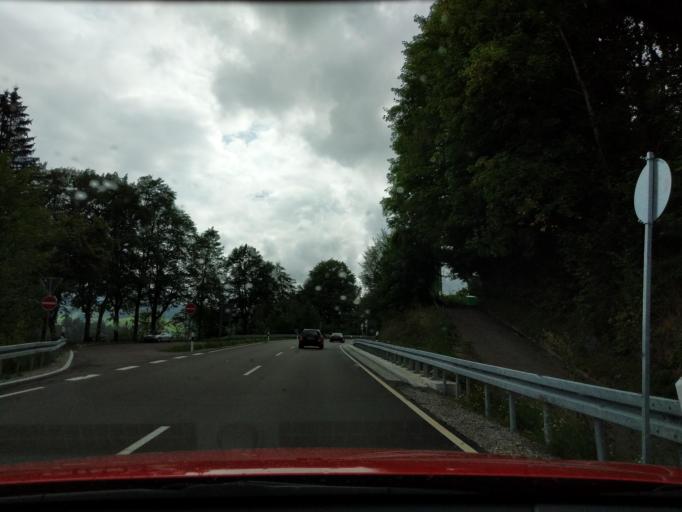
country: DE
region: Bavaria
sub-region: Swabia
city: Oberstaufen
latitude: 47.5500
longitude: 10.0384
